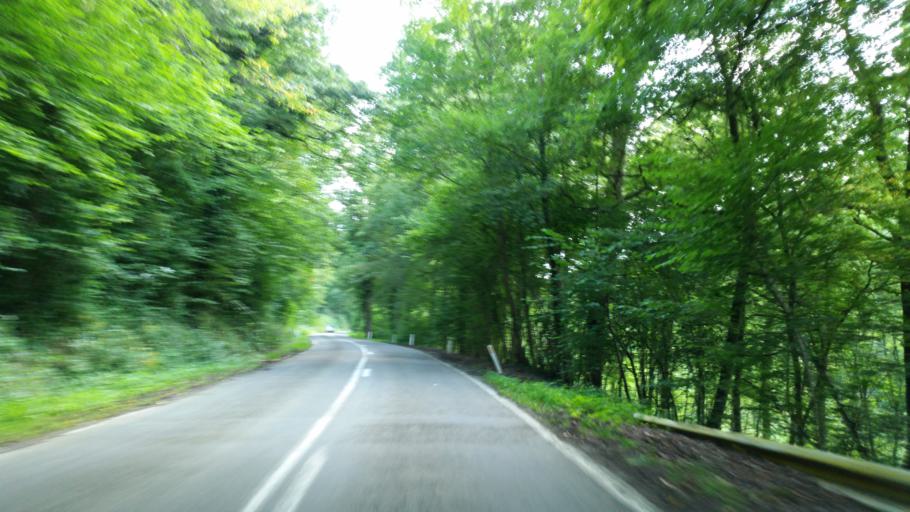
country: BE
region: Wallonia
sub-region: Province de Liege
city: Ouffet
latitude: 50.4026
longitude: 5.4364
